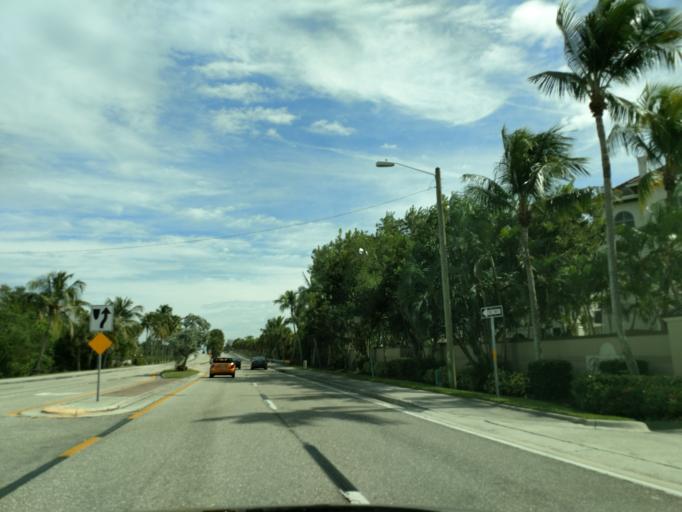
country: US
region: Florida
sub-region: Lee County
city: Bonita Springs
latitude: 26.3304
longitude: -81.8407
